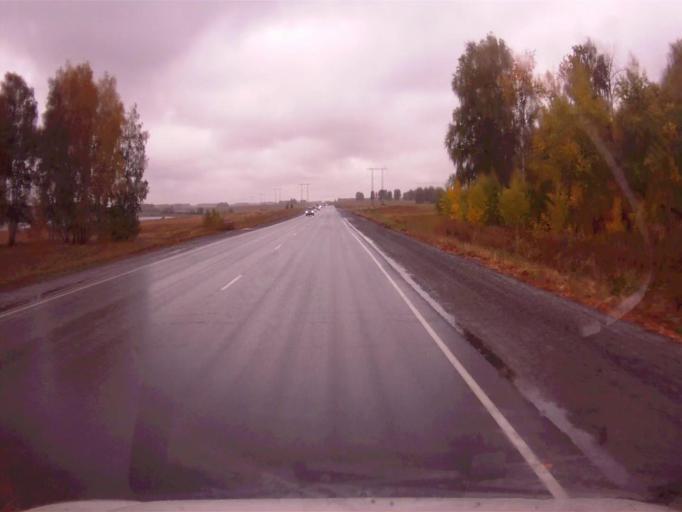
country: RU
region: Chelyabinsk
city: Roshchino
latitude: 55.3882
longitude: 61.1275
